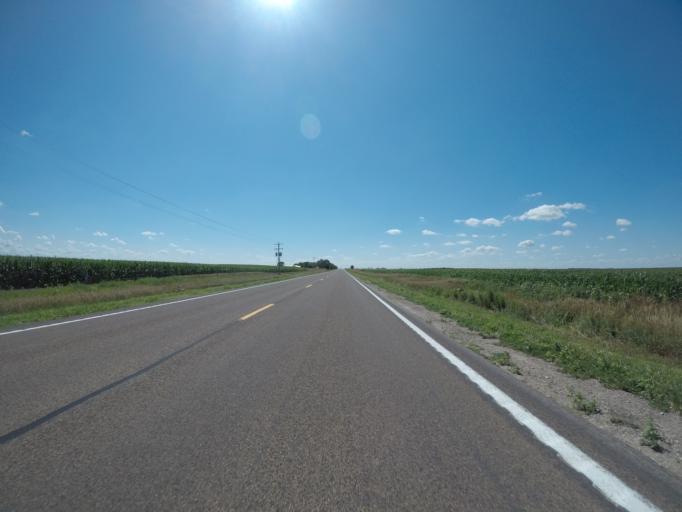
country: US
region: Nebraska
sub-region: Chase County
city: Imperial
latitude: 40.5376
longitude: -101.7261
